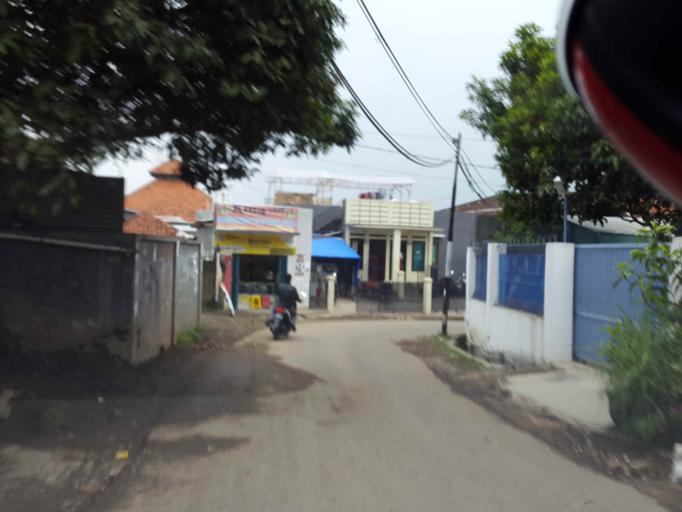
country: ID
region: West Java
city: Lembang
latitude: -6.8452
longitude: 107.5847
